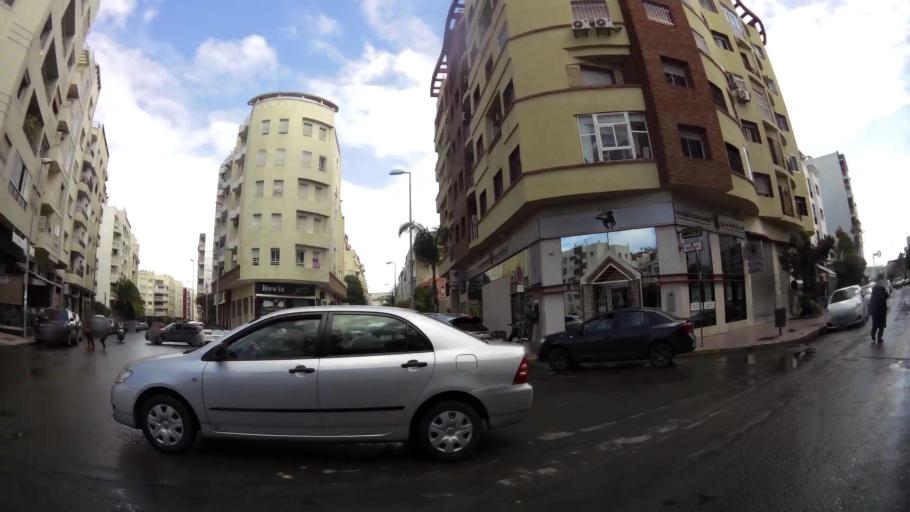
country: MA
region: Grand Casablanca
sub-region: Casablanca
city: Casablanca
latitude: 33.5727
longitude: -7.6384
